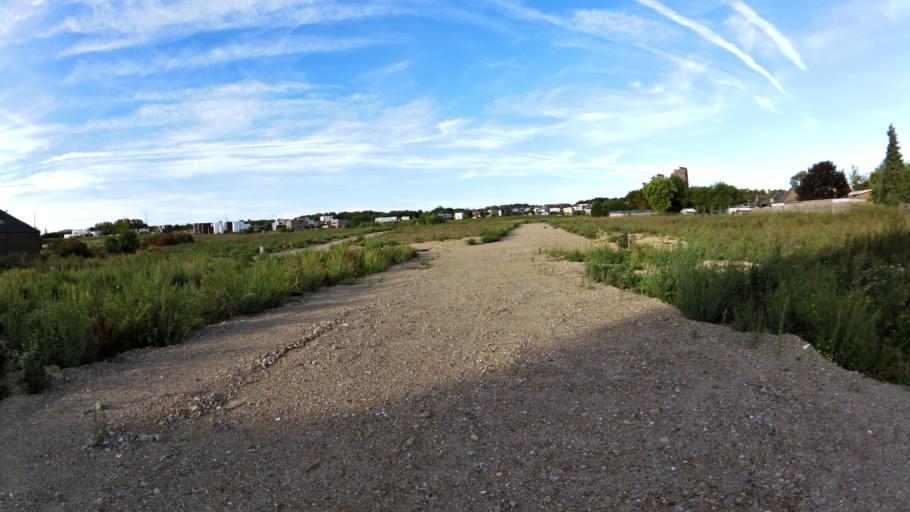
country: NL
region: Limburg
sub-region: Gemeente Heerlen
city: Heerlen
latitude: 50.8652
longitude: 6.0010
